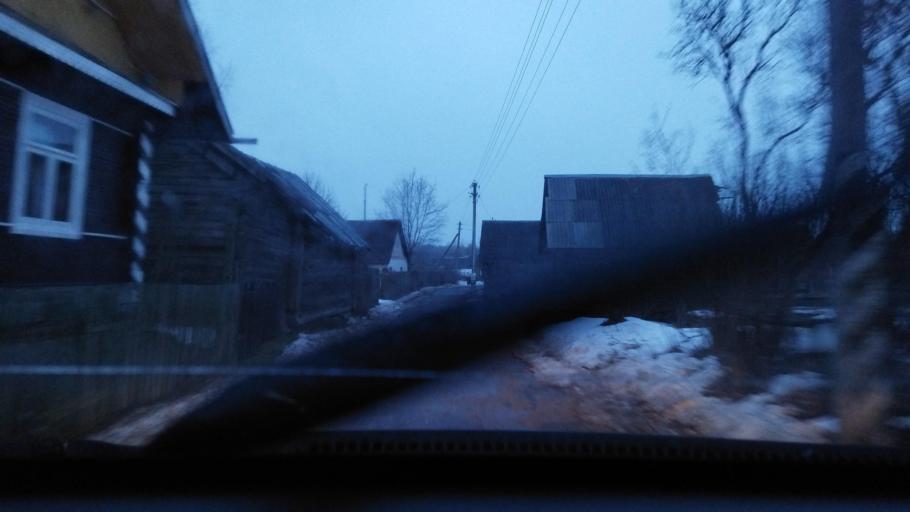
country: BY
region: Minsk
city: Svir
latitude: 54.9395
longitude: 26.4012
